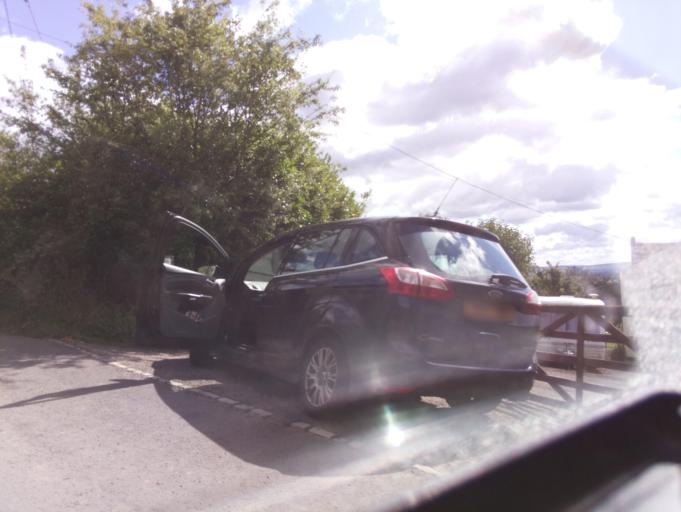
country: GB
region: England
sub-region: Gloucestershire
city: Cinderford
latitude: 51.8272
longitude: -2.4538
